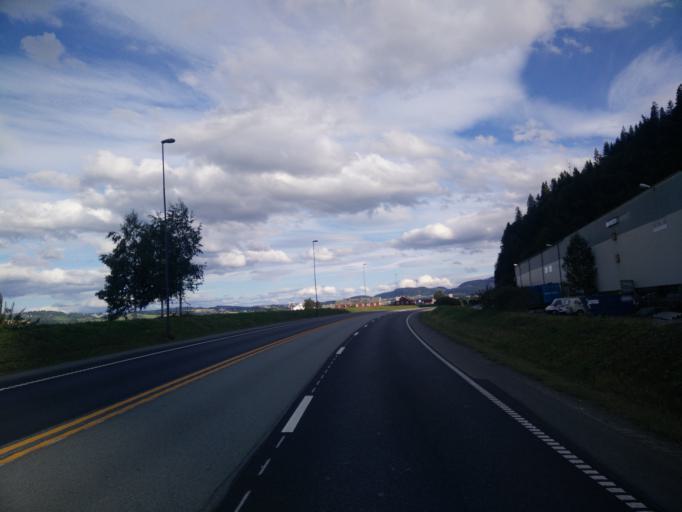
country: NO
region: Sor-Trondelag
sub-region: Melhus
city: Melhus
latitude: 63.3247
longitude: 10.2266
